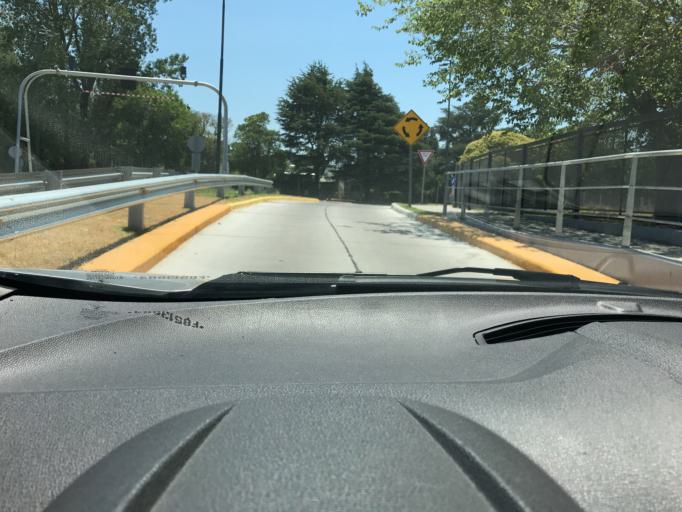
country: AR
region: Buenos Aires
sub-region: Partido de La Plata
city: La Plata
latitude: -34.8643
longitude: -58.0441
